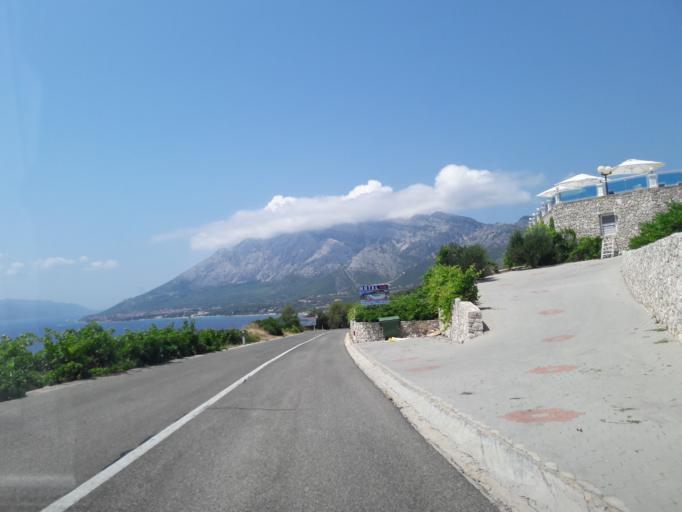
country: HR
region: Dubrovacko-Neretvanska
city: Orebic
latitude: 42.9750
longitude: 17.2325
